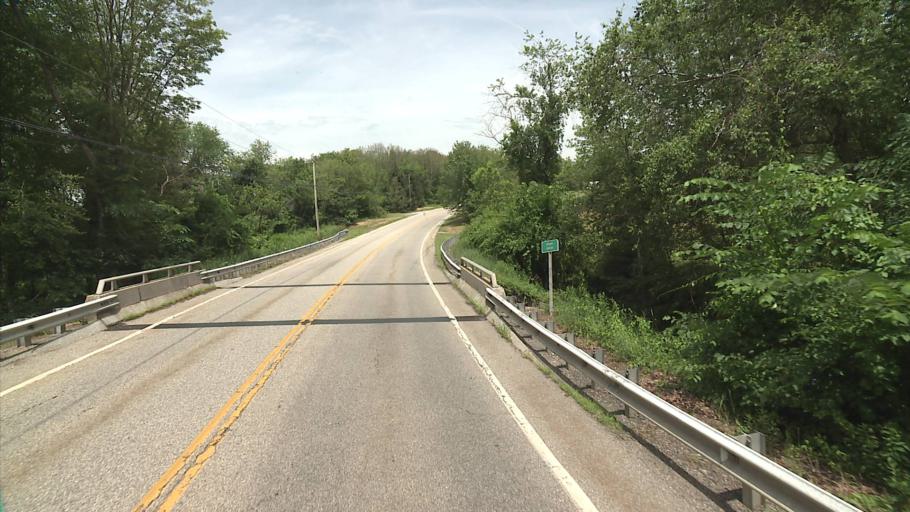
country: US
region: Connecticut
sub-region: New London County
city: Preston City
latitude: 41.5539
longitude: -71.9703
